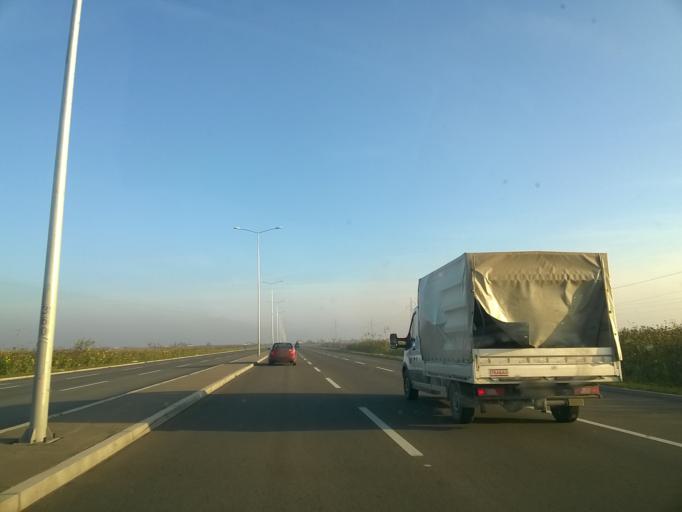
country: RS
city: Ovca
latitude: 44.8745
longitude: 20.5172
